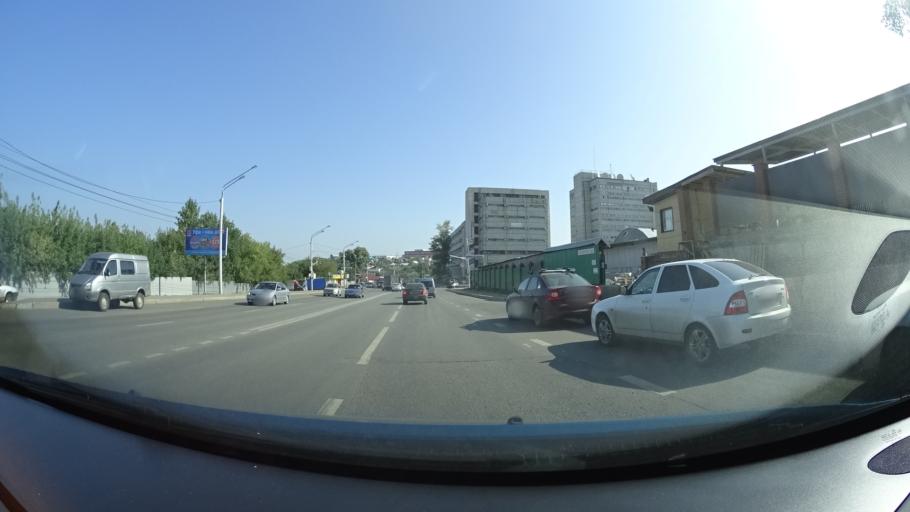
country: RU
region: Bashkortostan
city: Ufa
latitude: 54.7460
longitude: 55.9699
